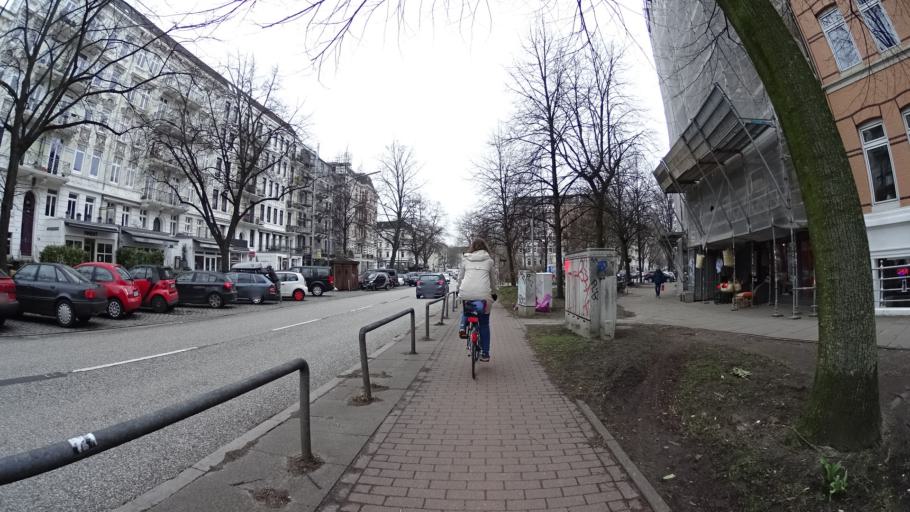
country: DE
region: Hamburg
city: Hamburg-Nord
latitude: 53.5818
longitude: 9.9799
